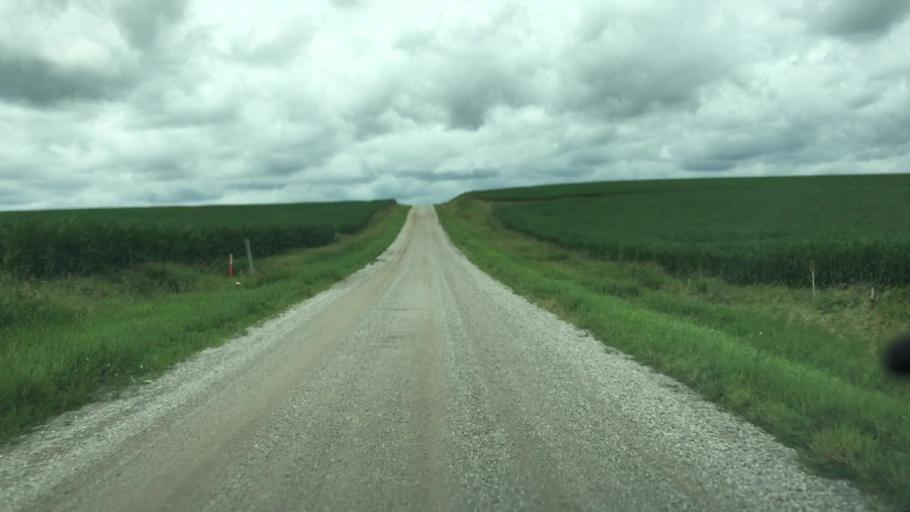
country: US
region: Iowa
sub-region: Jasper County
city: Monroe
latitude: 41.5953
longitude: -93.1007
